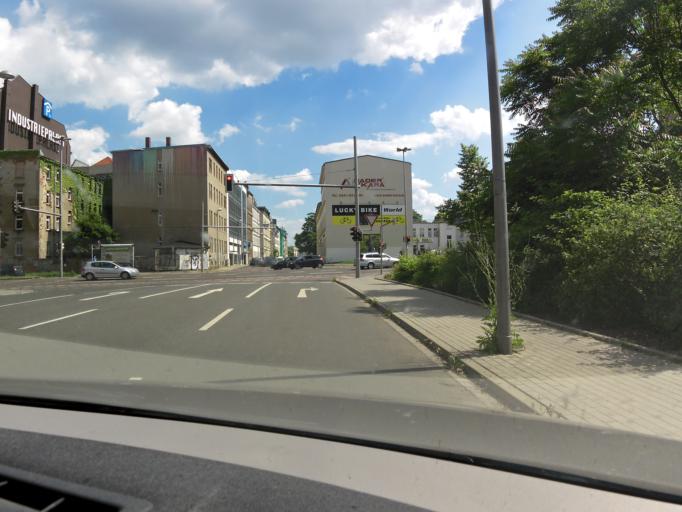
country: DE
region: Saxony
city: Leipzig
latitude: 51.3467
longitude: 12.3880
